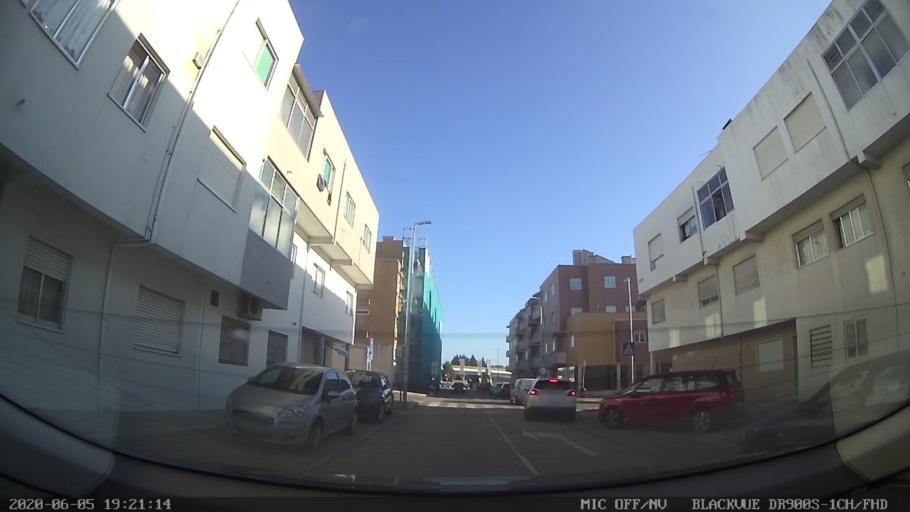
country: PT
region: Porto
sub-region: Gondomar
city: Baguim do Monte
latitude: 41.2065
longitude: -8.5473
